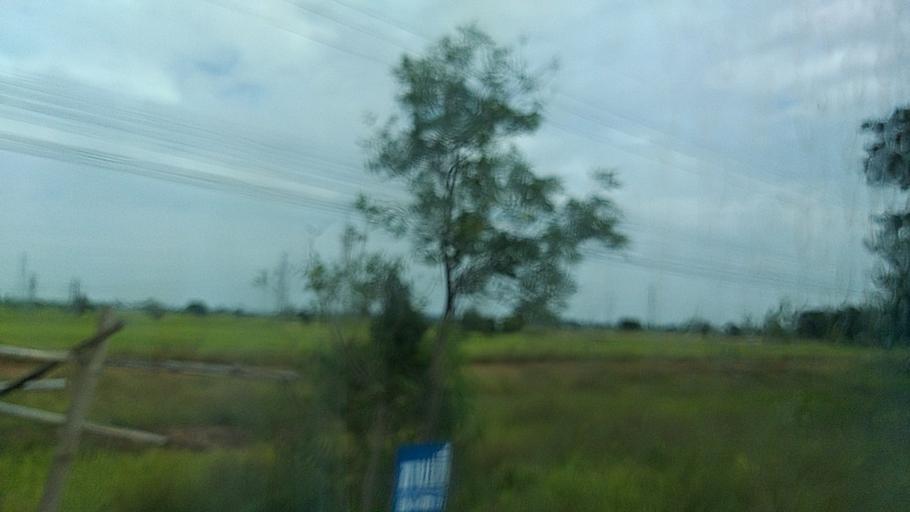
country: TH
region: Roi Et
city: Si Somdet
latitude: 16.1240
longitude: 103.4781
